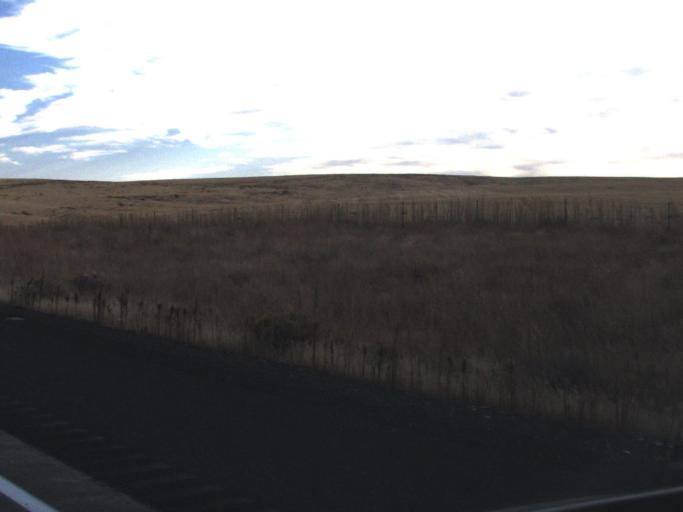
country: US
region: Washington
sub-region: Franklin County
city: Connell
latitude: 46.8015
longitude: -118.7314
